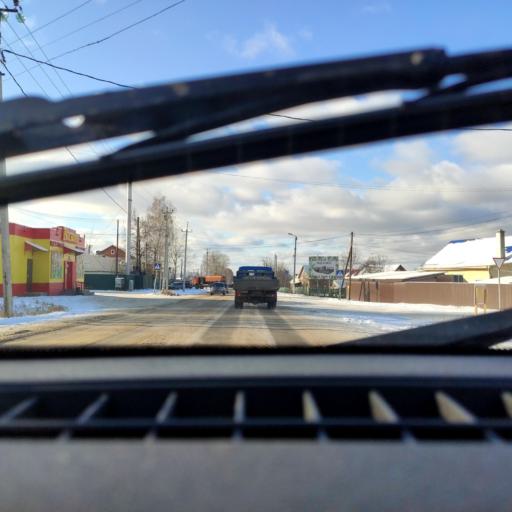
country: RU
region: Bashkortostan
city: Iglino
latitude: 54.8216
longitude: 56.4106
